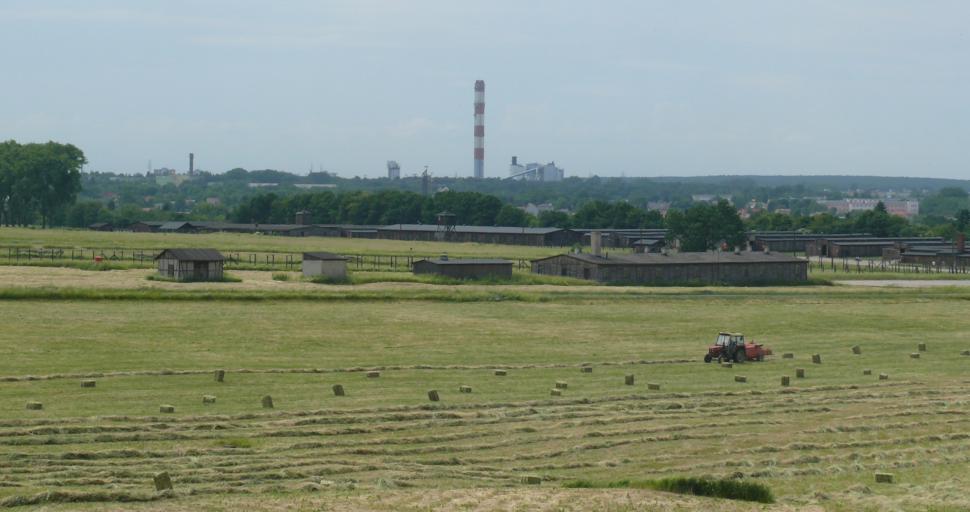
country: PL
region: Lublin Voivodeship
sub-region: Powiat lubelski
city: Lublin
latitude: 51.2253
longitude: 22.6040
